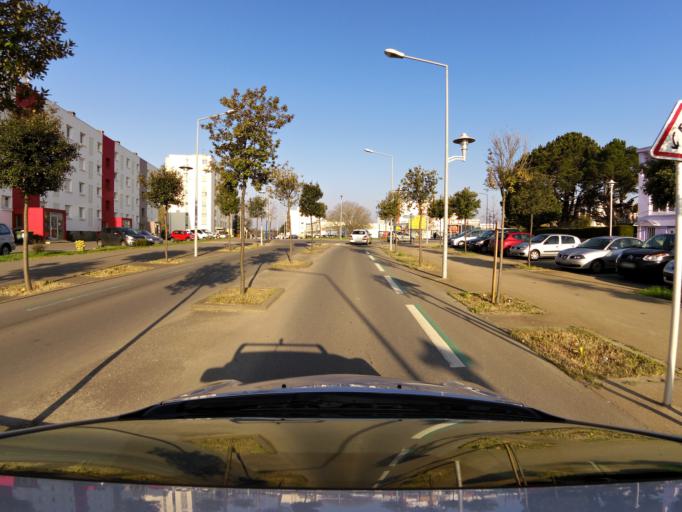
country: FR
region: Brittany
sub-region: Departement du Morbihan
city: Lorient
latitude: 47.7341
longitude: -3.3878
